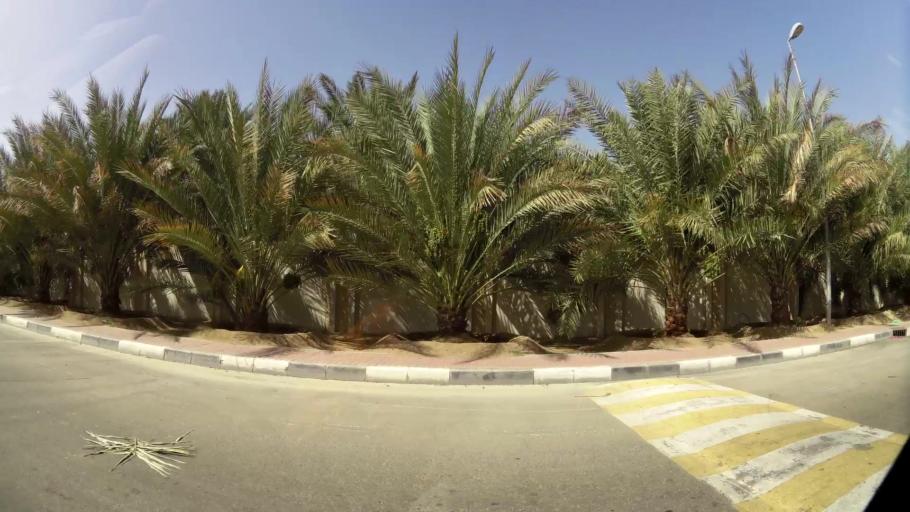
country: OM
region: Al Buraimi
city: Al Buraymi
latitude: 24.3063
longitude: 55.8021
